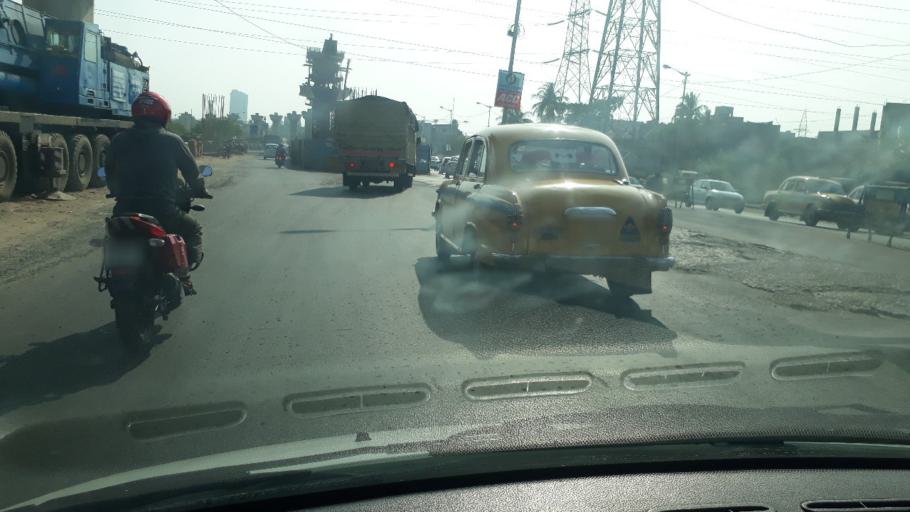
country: IN
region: West Bengal
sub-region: Kolkata
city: Kolkata
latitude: 22.5300
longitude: 88.3954
